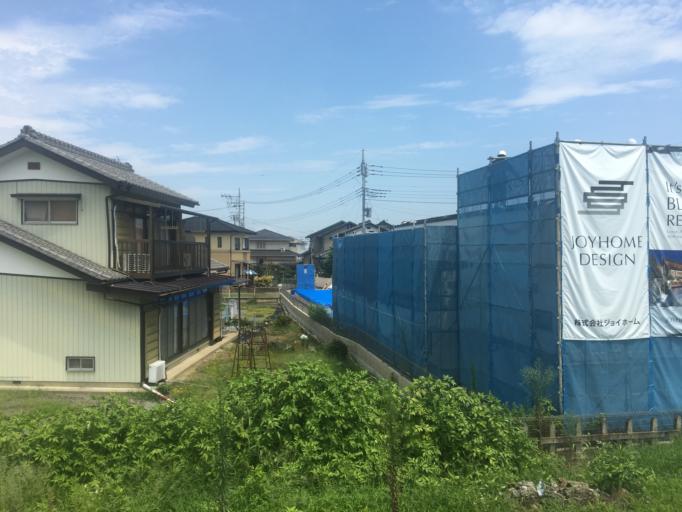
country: JP
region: Gunma
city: Fujioka
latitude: 36.2518
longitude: 139.0835
